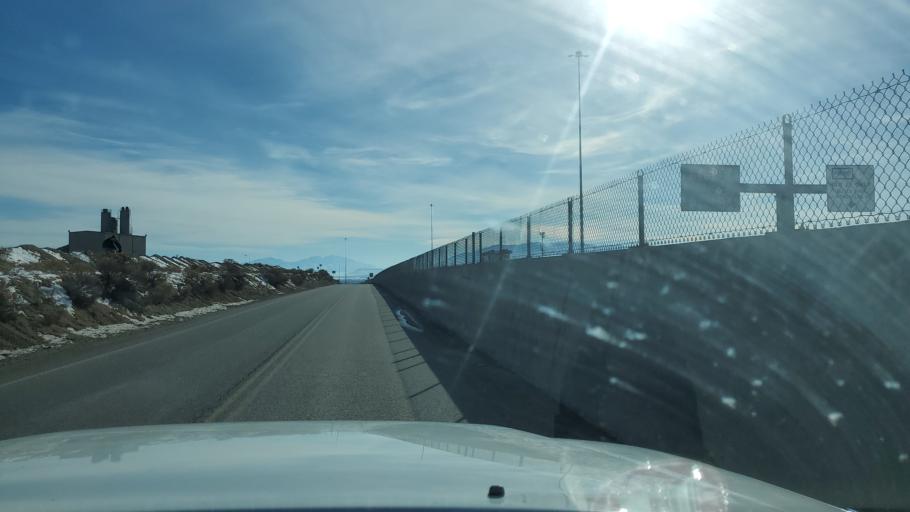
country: US
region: Utah
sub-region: Salt Lake County
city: Bluffdale
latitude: 40.4543
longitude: -111.9125
